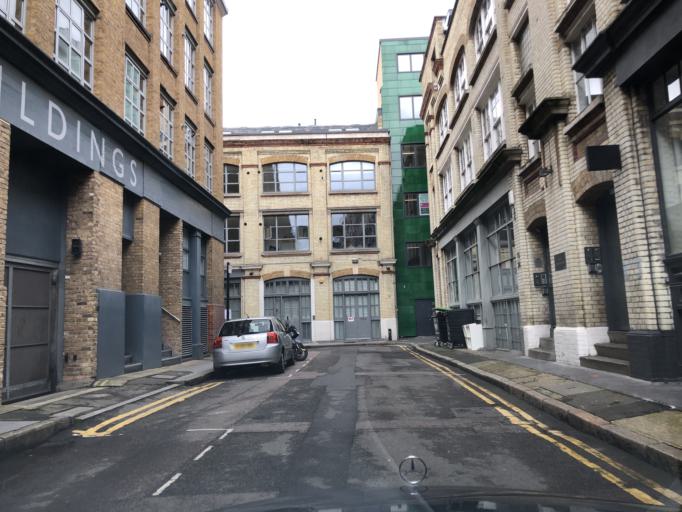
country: GB
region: England
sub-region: Greater London
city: Barbican
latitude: 51.5299
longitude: -0.0912
